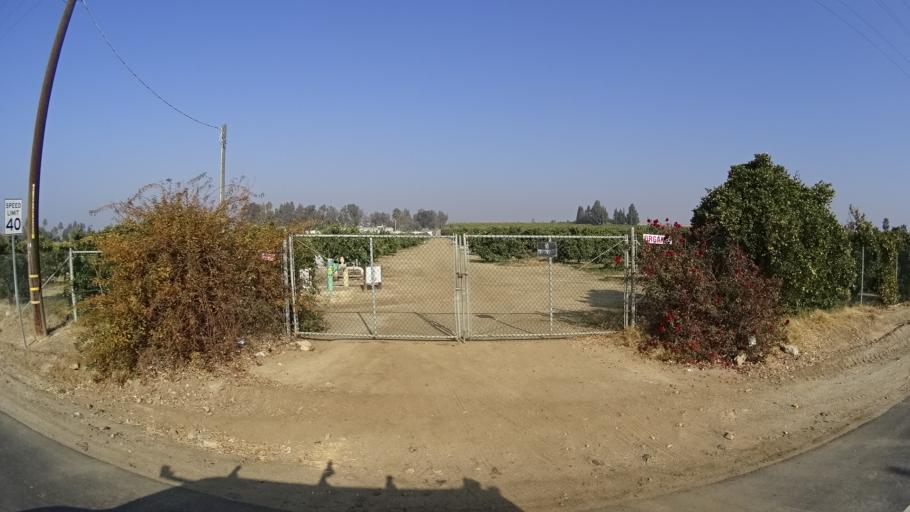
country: US
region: California
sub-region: Kern County
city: Lamont
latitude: 35.3618
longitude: -118.8941
